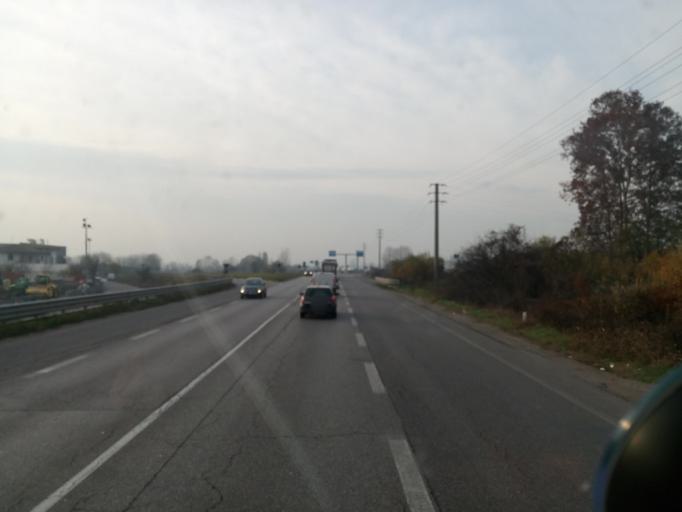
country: IT
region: Lombardy
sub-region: Provincia di Brescia
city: Montichiari
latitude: 45.4007
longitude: 10.3940
